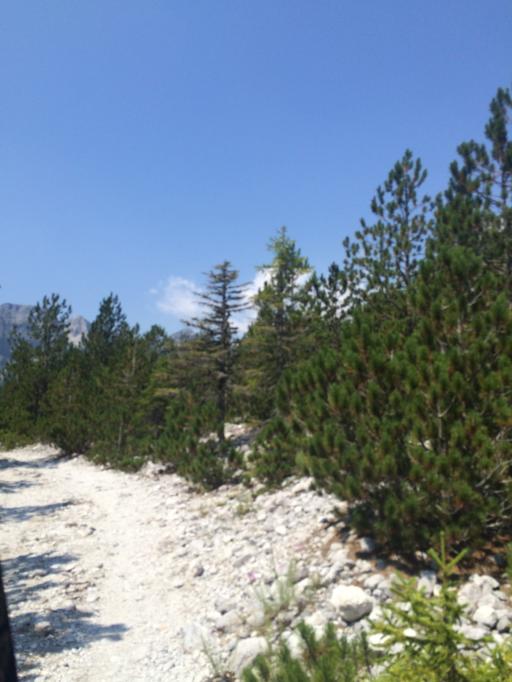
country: AL
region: Kukes
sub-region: Rrethi i Tropojes
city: Valbone
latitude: 42.4151
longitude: 19.8541
